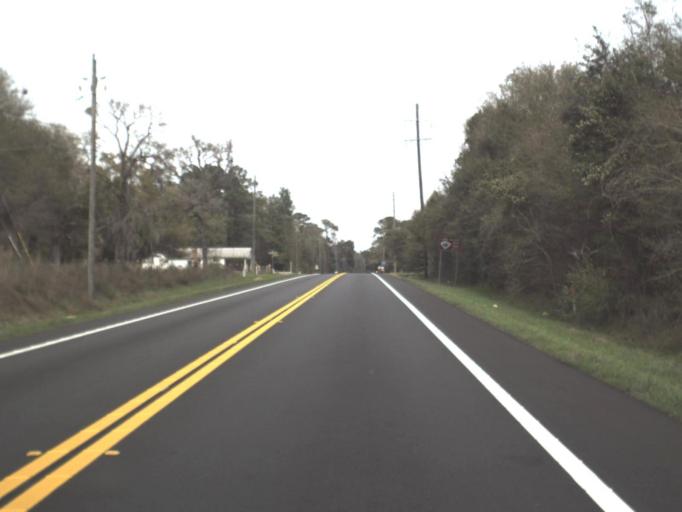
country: US
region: Florida
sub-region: Gadsden County
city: Midway
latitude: 30.4326
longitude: -84.5268
